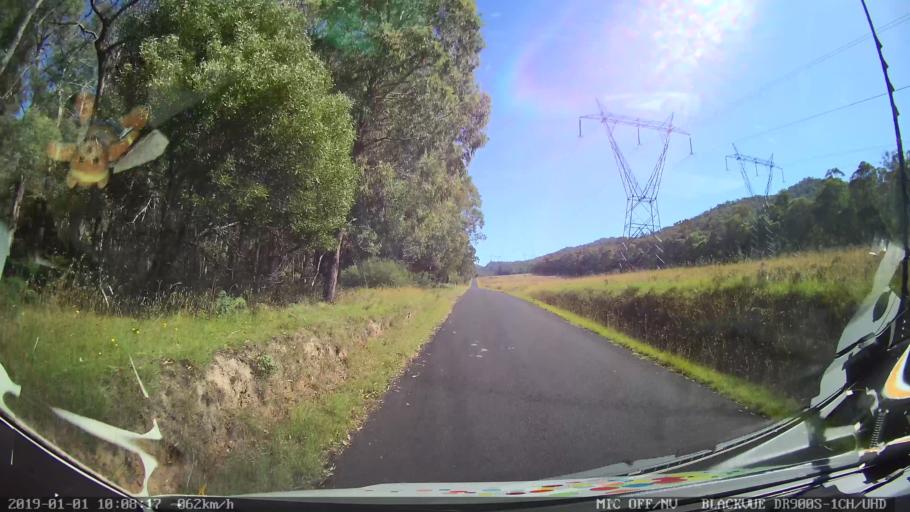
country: AU
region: New South Wales
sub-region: Snowy River
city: Jindabyne
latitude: -36.1609
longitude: 148.1574
